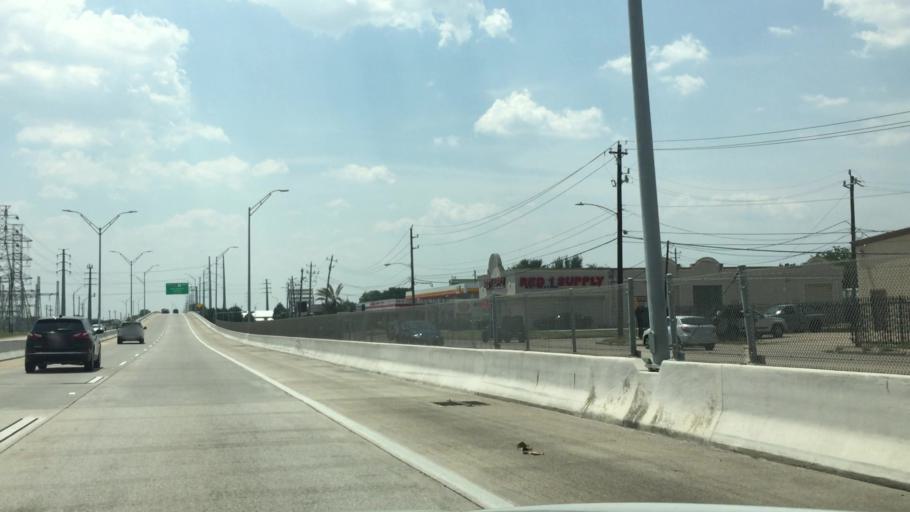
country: US
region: Texas
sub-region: Harris County
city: Piney Point Village
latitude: 29.7204
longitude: -95.5318
